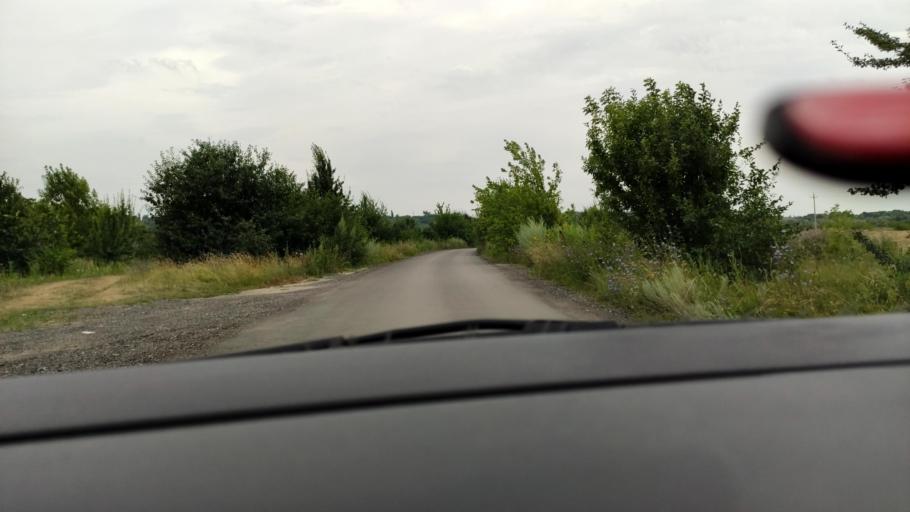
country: RU
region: Voronezj
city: Ramon'
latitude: 51.8973
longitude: 39.3506
